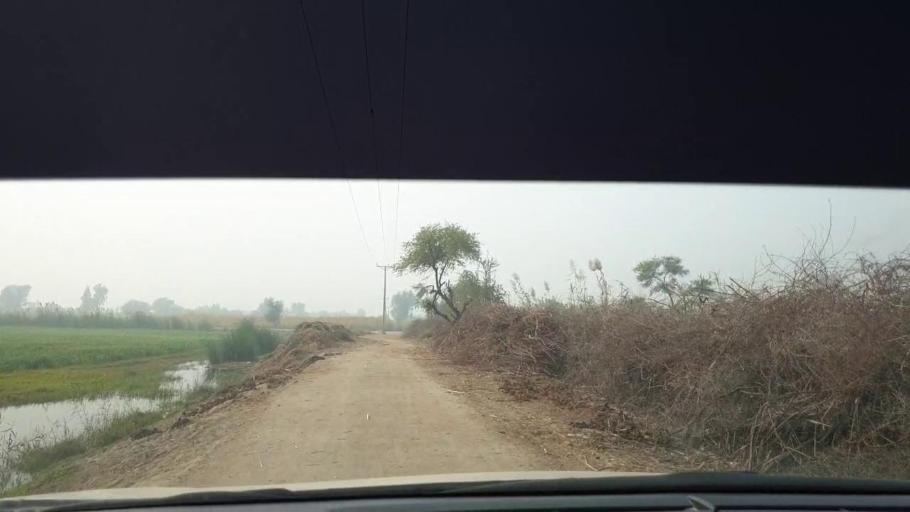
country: PK
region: Sindh
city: Berani
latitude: 25.8429
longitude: 68.8360
